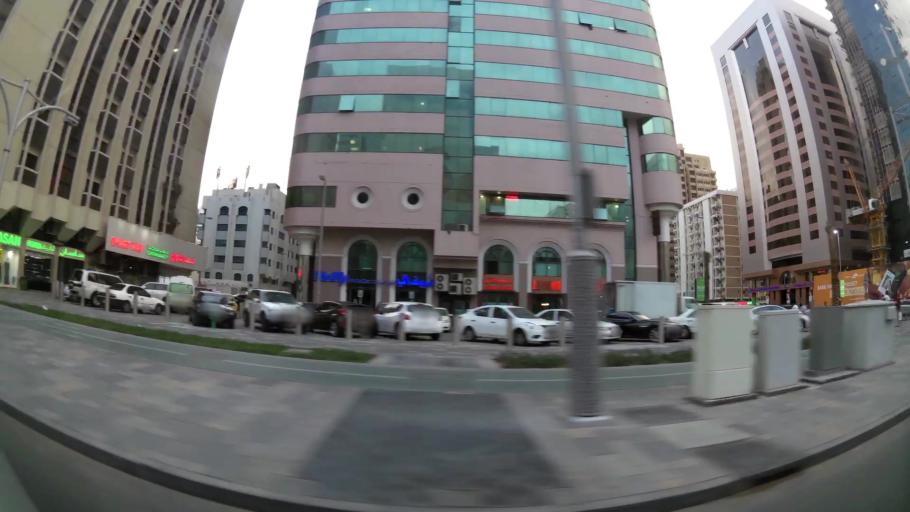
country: AE
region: Abu Dhabi
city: Abu Dhabi
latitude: 24.4961
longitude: 54.3731
